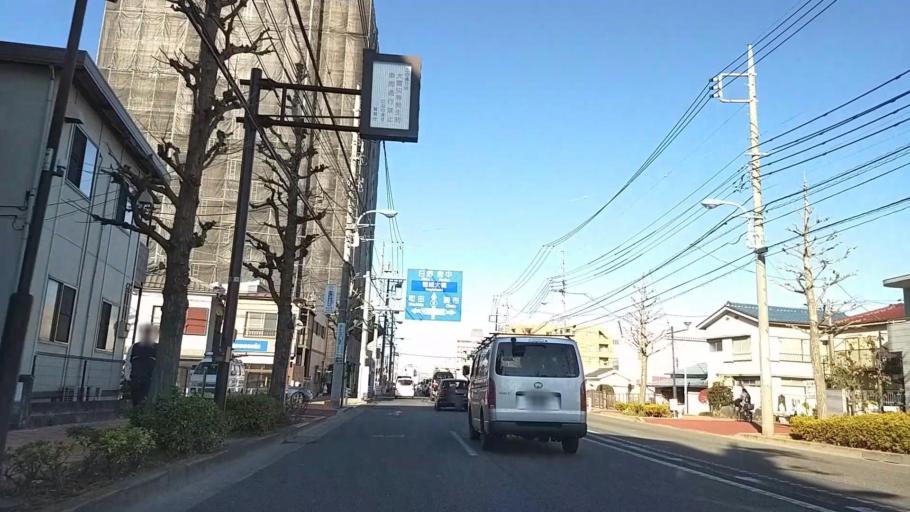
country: JP
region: Tokyo
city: Chofugaoka
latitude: 35.6398
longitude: 139.5214
